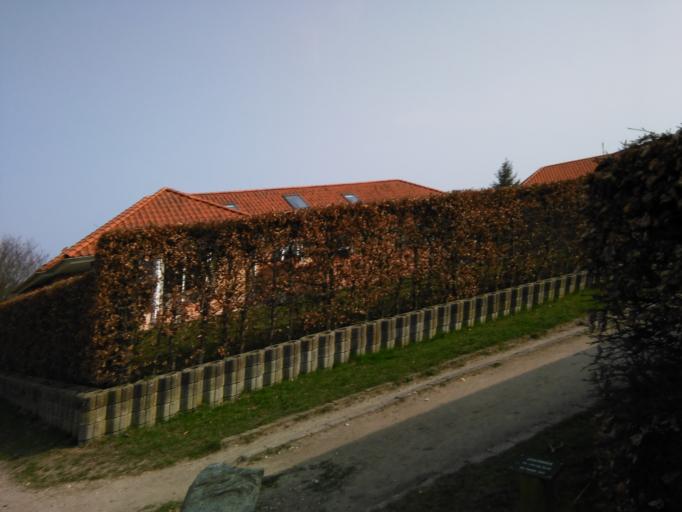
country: DK
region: Central Jutland
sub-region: Arhus Kommune
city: Beder
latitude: 56.0645
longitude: 10.2216
